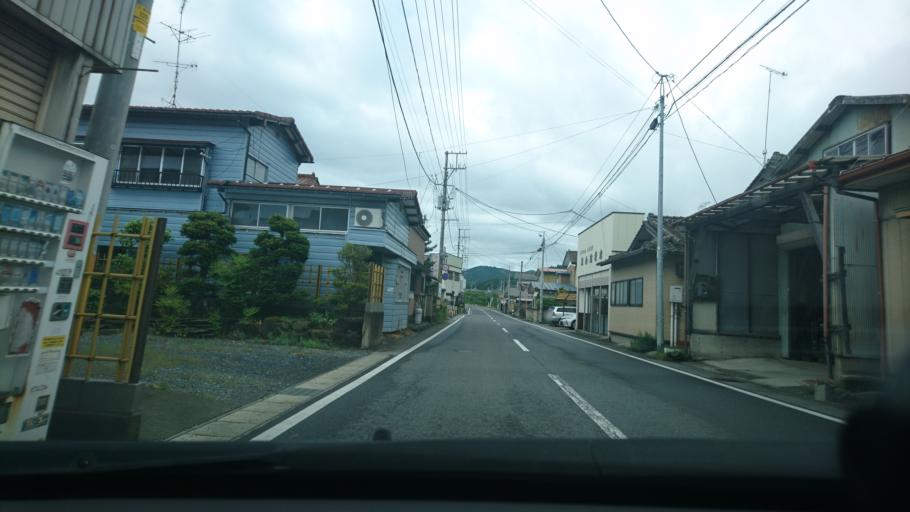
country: JP
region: Miyagi
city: Wakuya
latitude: 38.6064
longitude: 141.3009
